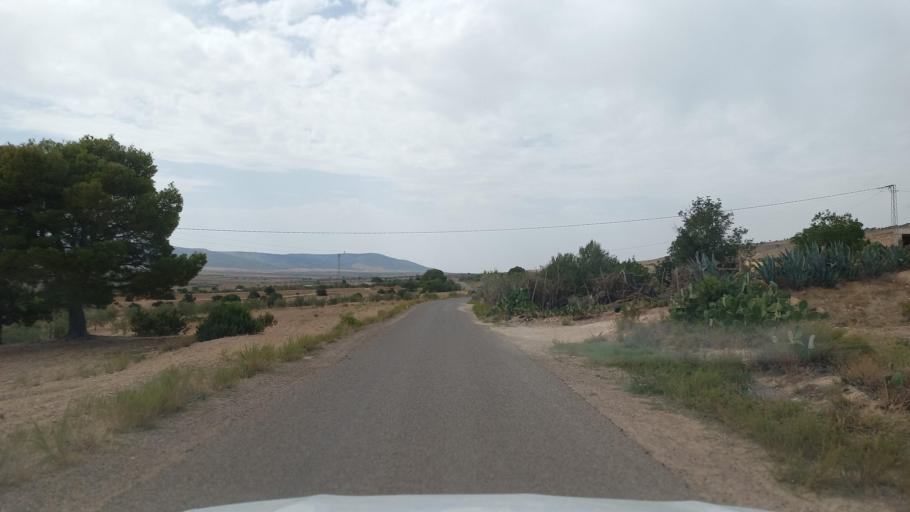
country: TN
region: Al Qasrayn
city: Kasserine
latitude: 35.3721
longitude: 8.8954
